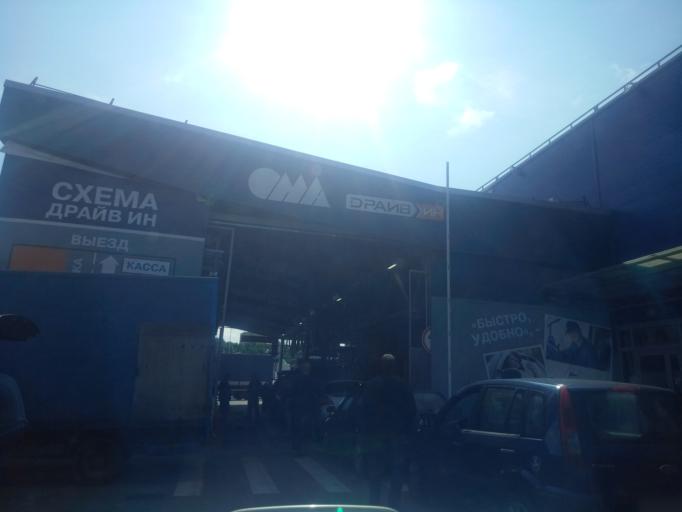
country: BY
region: Minsk
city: Shchomyslitsa
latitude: 53.8428
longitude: 27.4779
